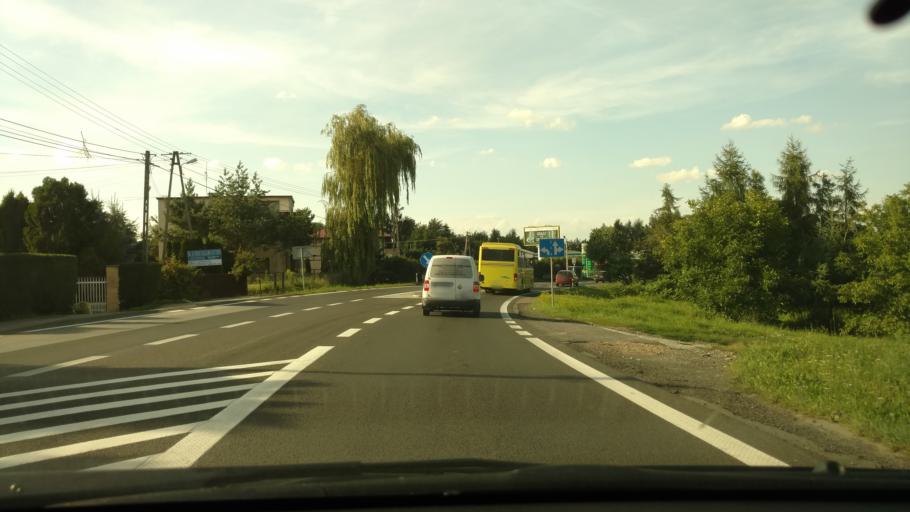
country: PL
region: Lesser Poland Voivodeship
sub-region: Powiat krakowski
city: Michalowice
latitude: 50.1318
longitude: 19.9670
